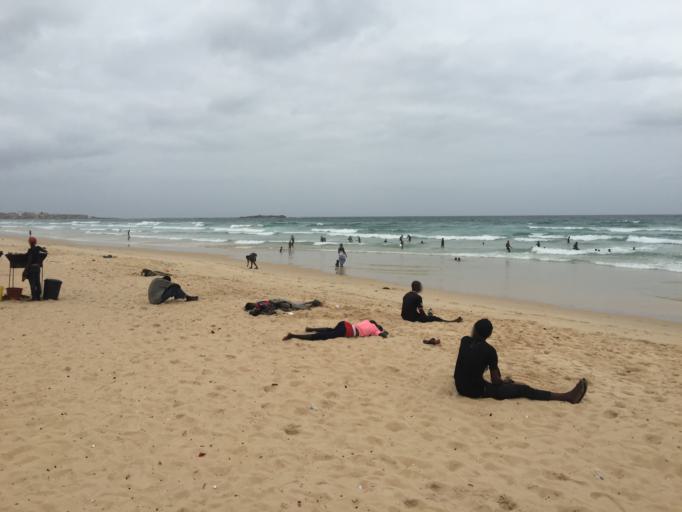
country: SN
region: Dakar
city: Grand Dakar
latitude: 14.7626
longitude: -17.4622
